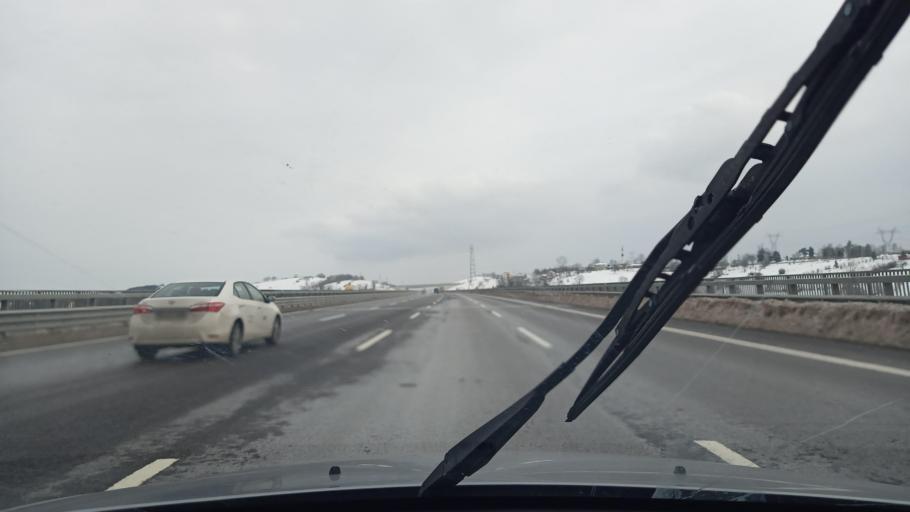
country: TR
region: Kocaeli
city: Korfez
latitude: 40.8652
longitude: 29.8025
